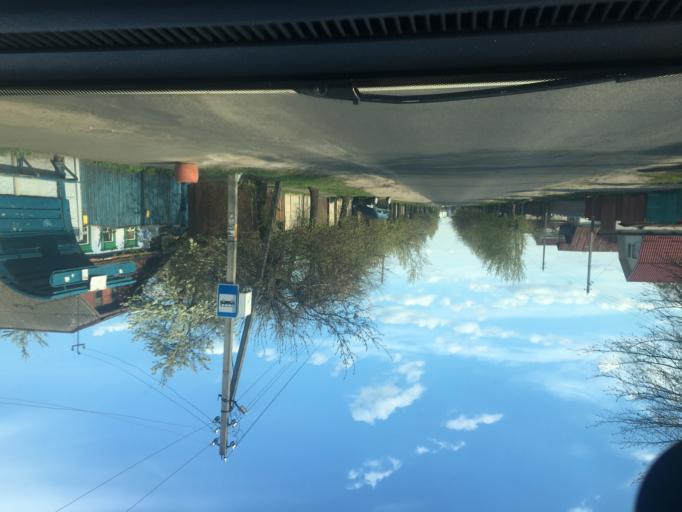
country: BY
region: Mogilev
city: Babruysk
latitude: 53.1490
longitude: 29.1924
